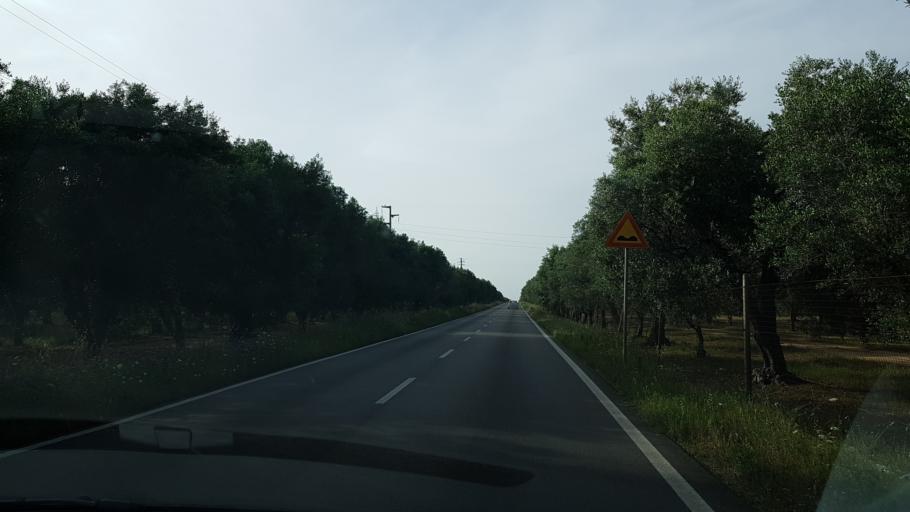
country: IT
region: Apulia
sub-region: Provincia di Brindisi
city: San Pancrazio Salentino
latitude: 40.3586
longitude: 17.8432
